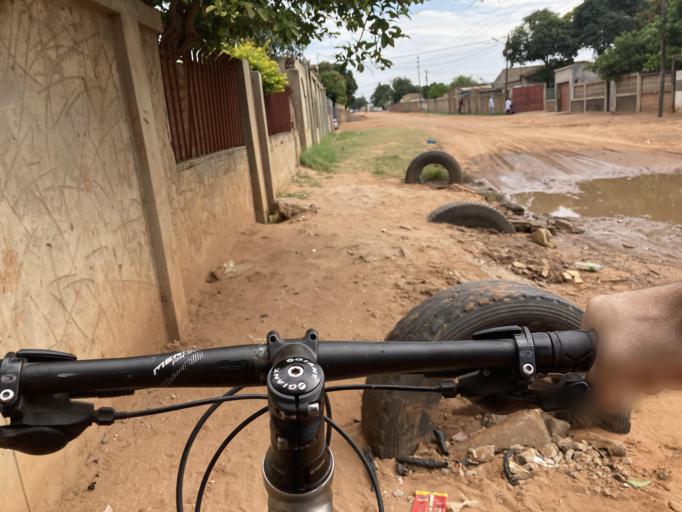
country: MZ
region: Maputo City
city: Maputo
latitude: -25.8937
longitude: 32.6078
